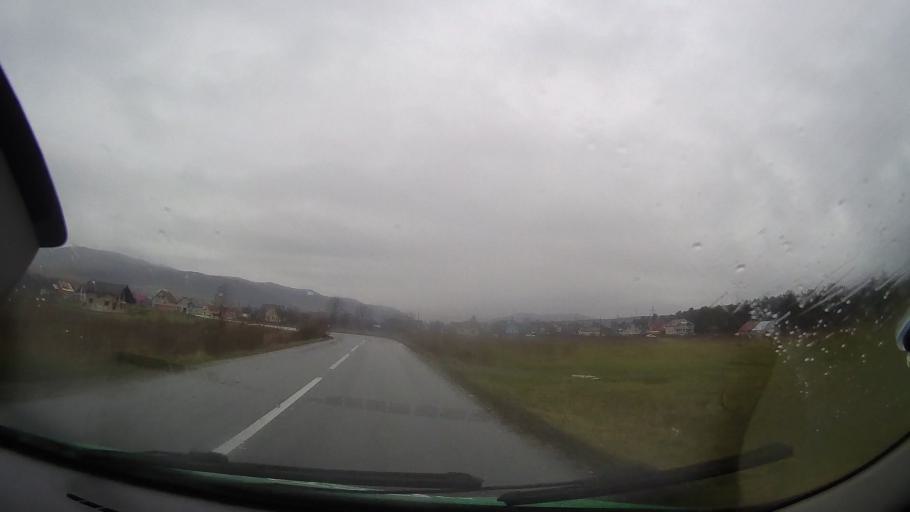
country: RO
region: Bistrita-Nasaud
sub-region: Comuna Mariselu
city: Mariselu
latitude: 47.0304
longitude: 24.4896
